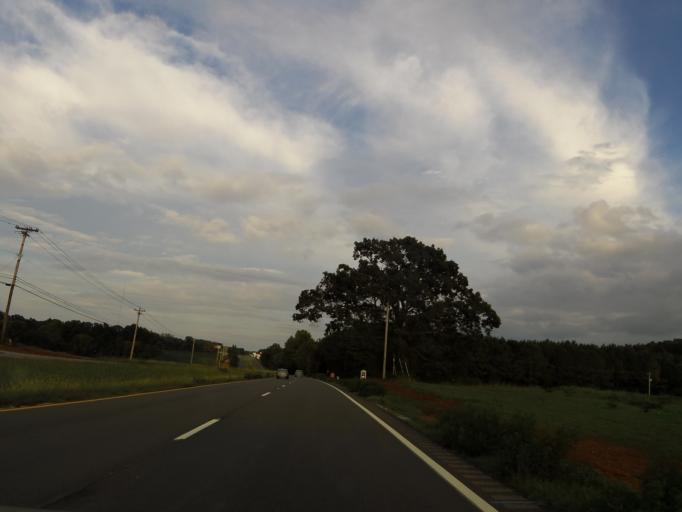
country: US
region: Alabama
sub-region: Madison County
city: Madison
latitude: 34.7493
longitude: -86.8079
